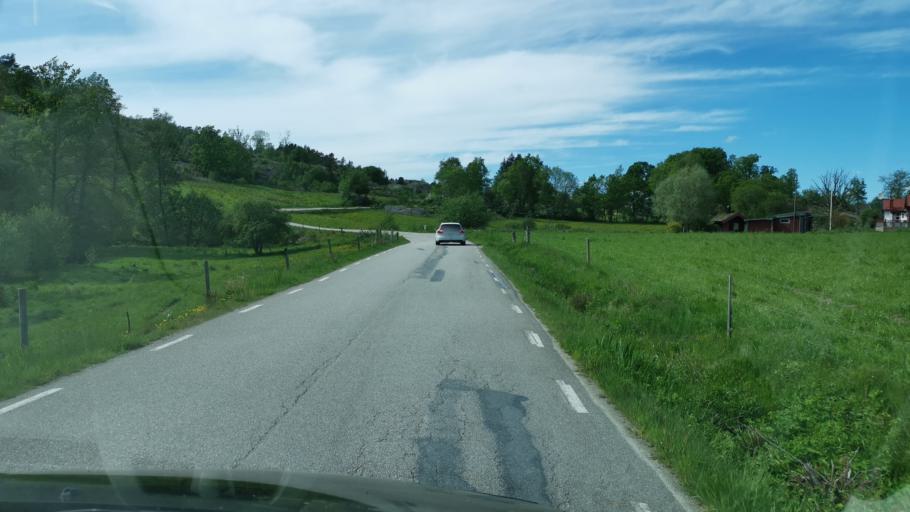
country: SE
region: Vaestra Goetaland
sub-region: Orust
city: Henan
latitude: 58.2704
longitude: 11.6035
